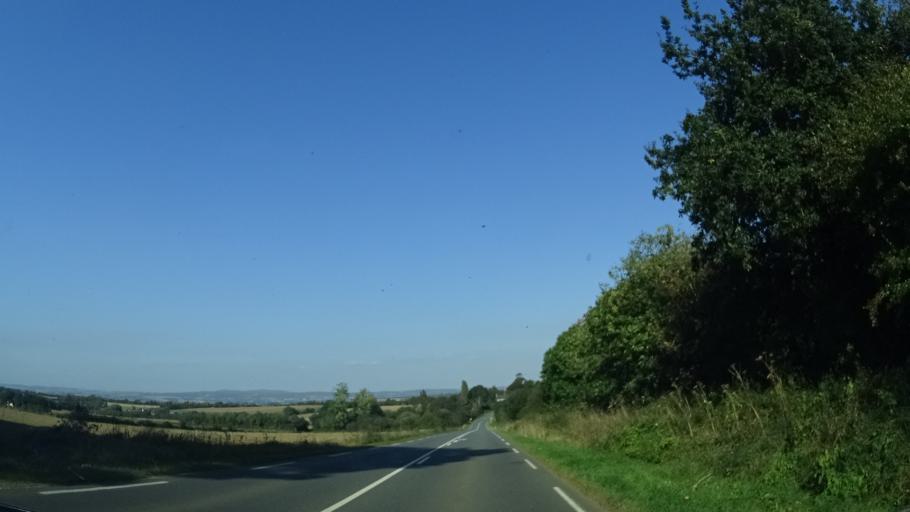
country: FR
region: Brittany
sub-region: Departement du Finistere
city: Plonevez-Porzay
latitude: 48.0989
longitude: -4.2550
